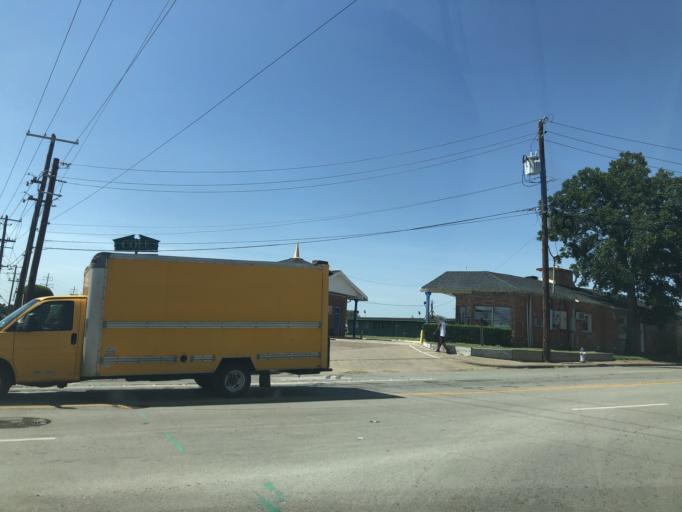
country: US
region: Texas
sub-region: Dallas County
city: University Park
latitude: 32.8261
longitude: -96.8547
